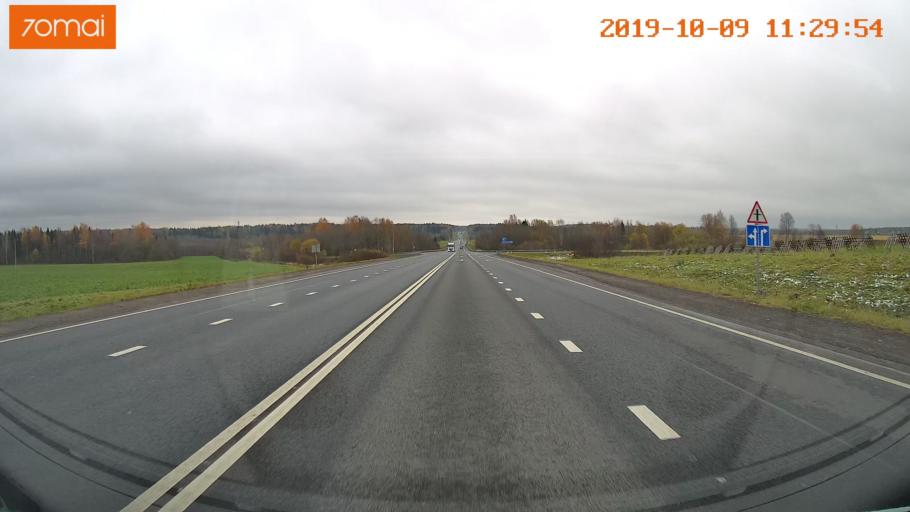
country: RU
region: Vologda
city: Vologda
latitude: 59.0583
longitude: 40.0635
